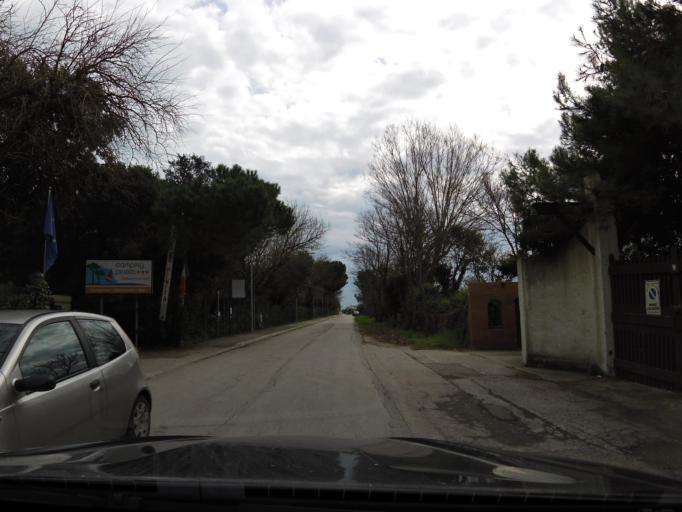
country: IT
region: The Marches
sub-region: Provincia di Macerata
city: Porto Recanati
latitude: 43.4170
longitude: 13.6722
